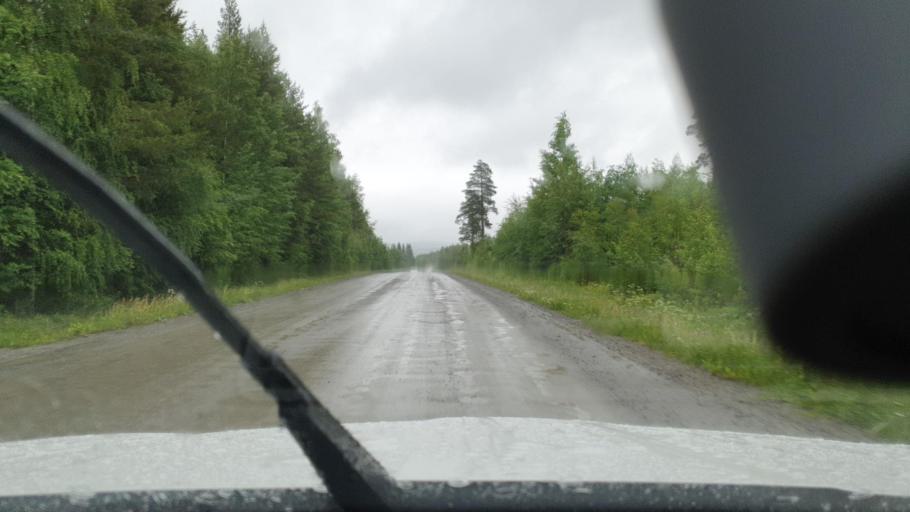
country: SE
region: Vaesterbotten
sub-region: Skelleftea Kommun
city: Burtraesk
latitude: 64.3581
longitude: 20.4457
